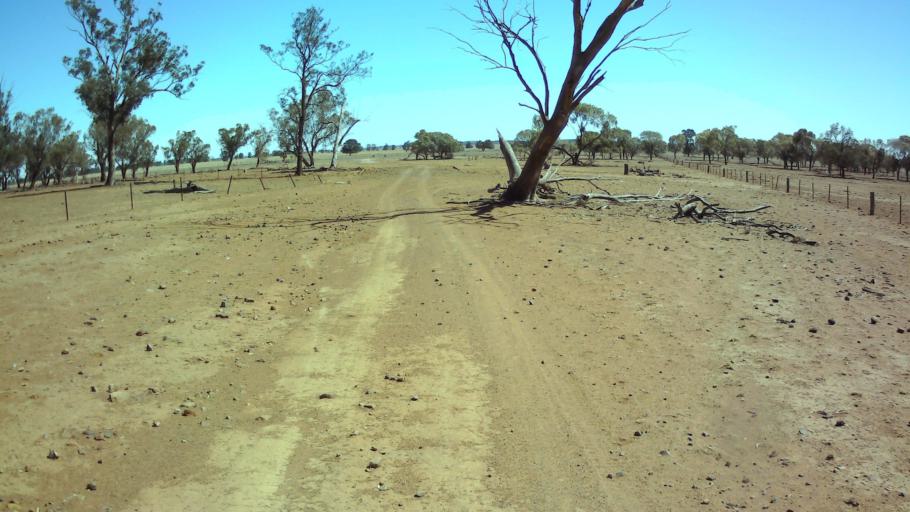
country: AU
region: New South Wales
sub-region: Forbes
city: Forbes
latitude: -33.7277
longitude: 147.6658
